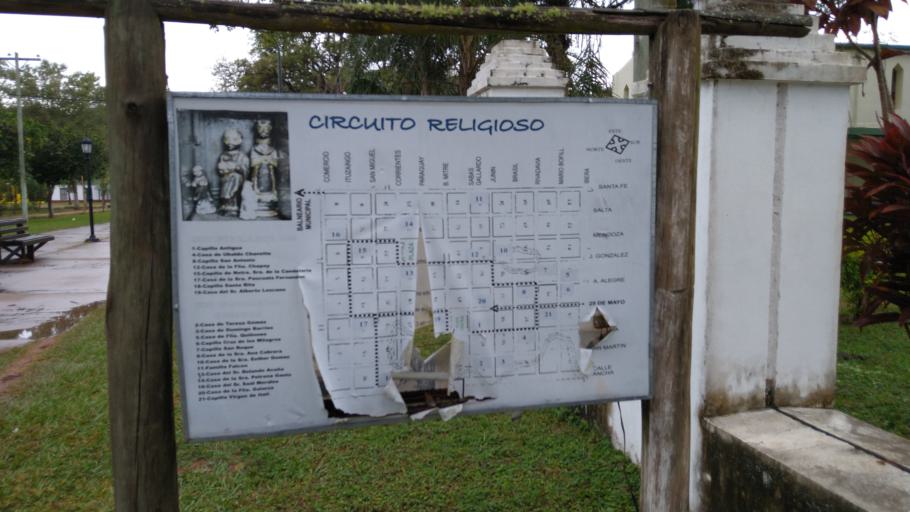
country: AR
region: Corrientes
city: Loreto
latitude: -27.7708
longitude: -57.2800
